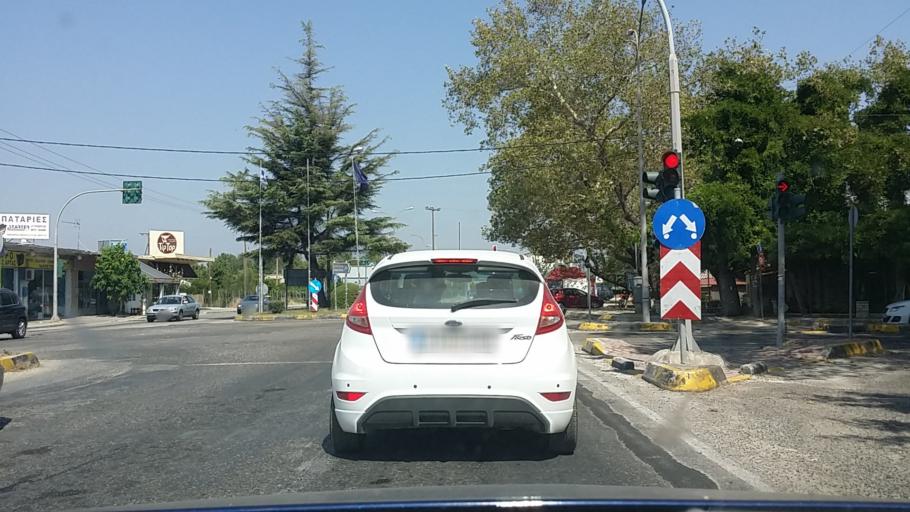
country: GR
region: Epirus
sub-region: Nomos Artas
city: Arta
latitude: 39.1509
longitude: 20.9733
